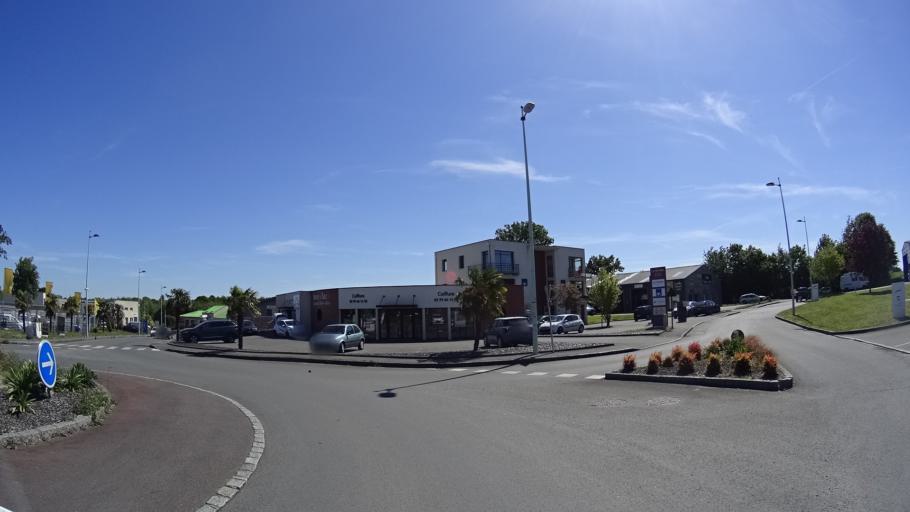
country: FR
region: Brittany
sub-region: Departement d'Ille-et-Vilaine
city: Melesse
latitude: 48.2138
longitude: -1.7027
